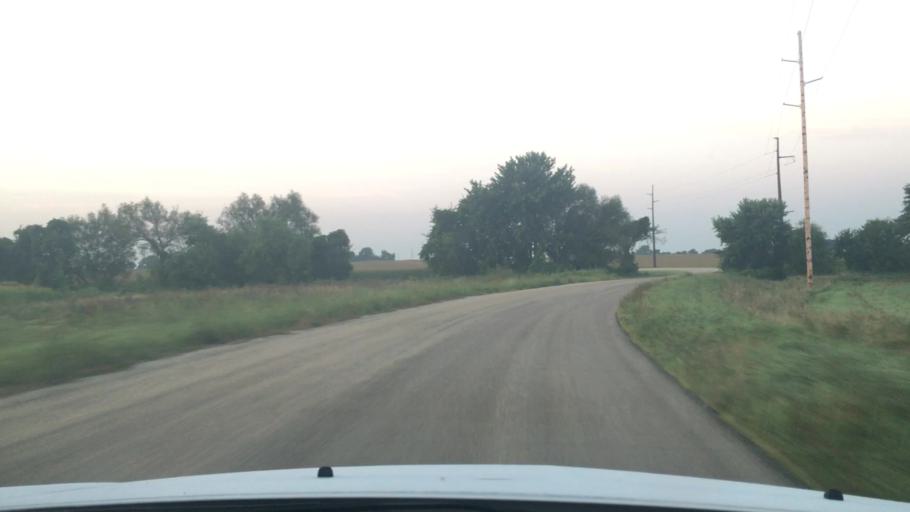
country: US
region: Illinois
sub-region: Ogle County
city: Rochelle
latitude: 41.8920
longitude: -88.9998
